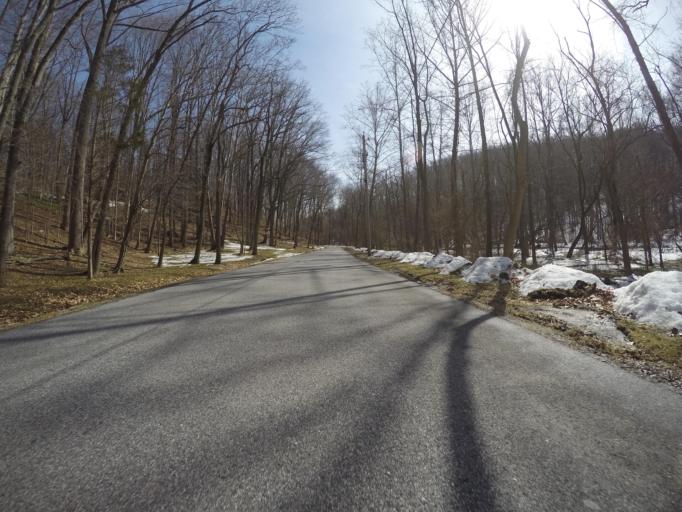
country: US
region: Maryland
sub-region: Baltimore County
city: Hunt Valley
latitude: 39.5039
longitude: -76.6523
